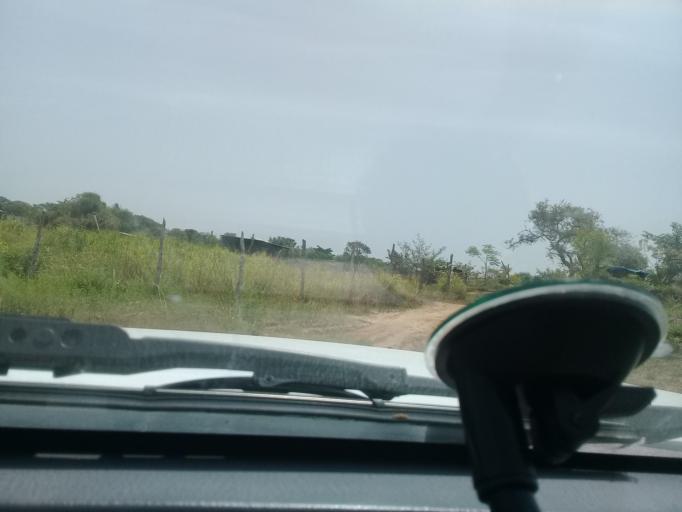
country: MX
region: Veracruz
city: Anahuac
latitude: 22.2275
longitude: -97.8266
